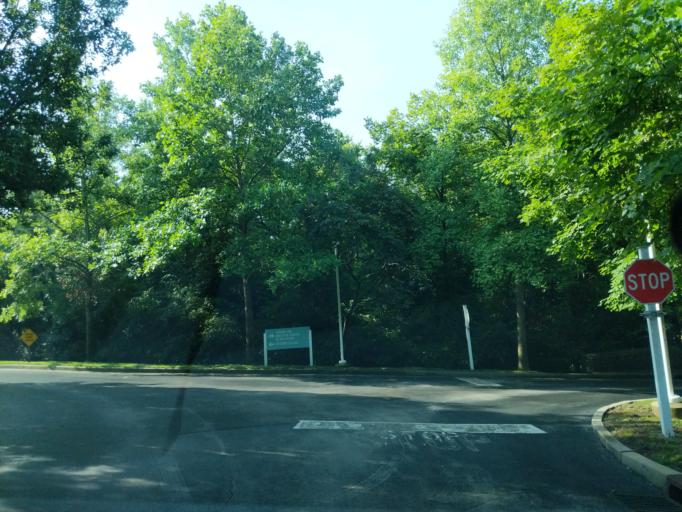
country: US
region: Tennessee
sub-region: Davidson County
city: Goodlettsville
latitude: 36.3093
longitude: -86.7007
